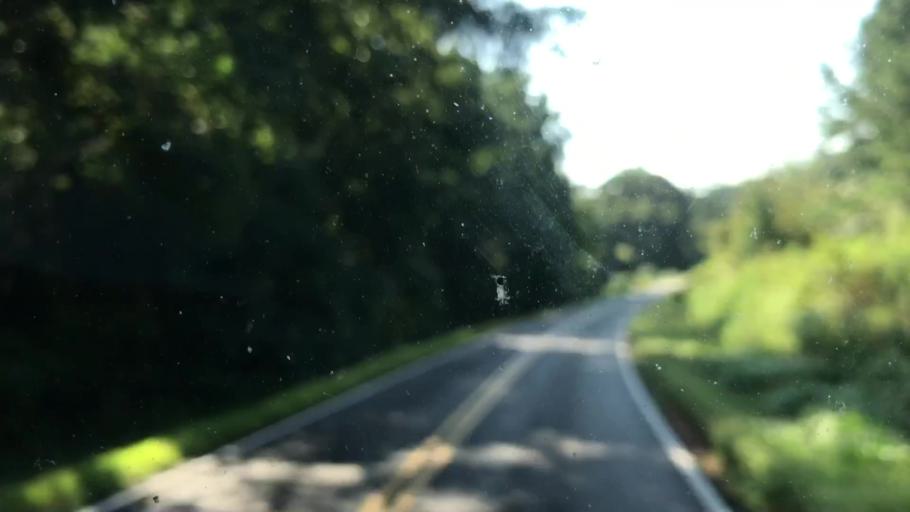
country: US
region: Georgia
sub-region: Walton County
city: Monroe
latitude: 33.8562
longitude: -83.7889
